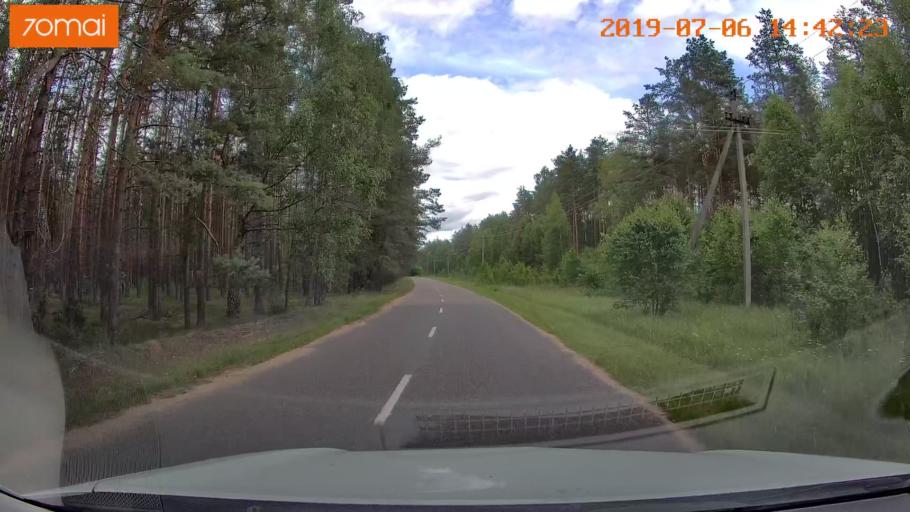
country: BY
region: Minsk
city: Ivyanyets
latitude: 53.9408
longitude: 26.6883
